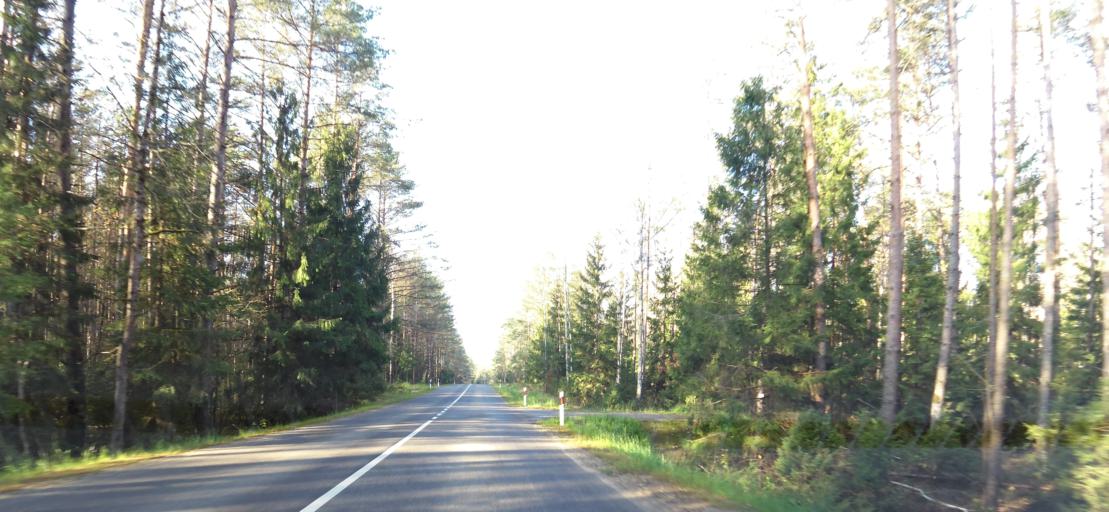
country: LT
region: Vilnius County
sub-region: Trakai
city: Rudiskes
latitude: 54.5099
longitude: 24.9052
